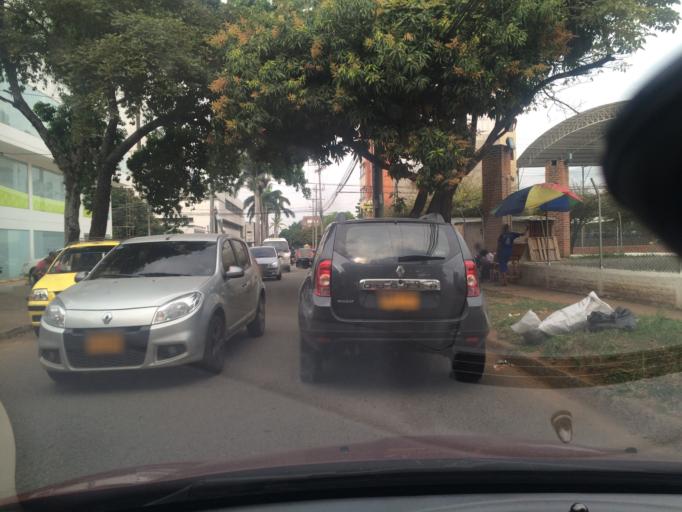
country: CO
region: Valle del Cauca
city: Cali
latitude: 3.4149
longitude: -76.5395
